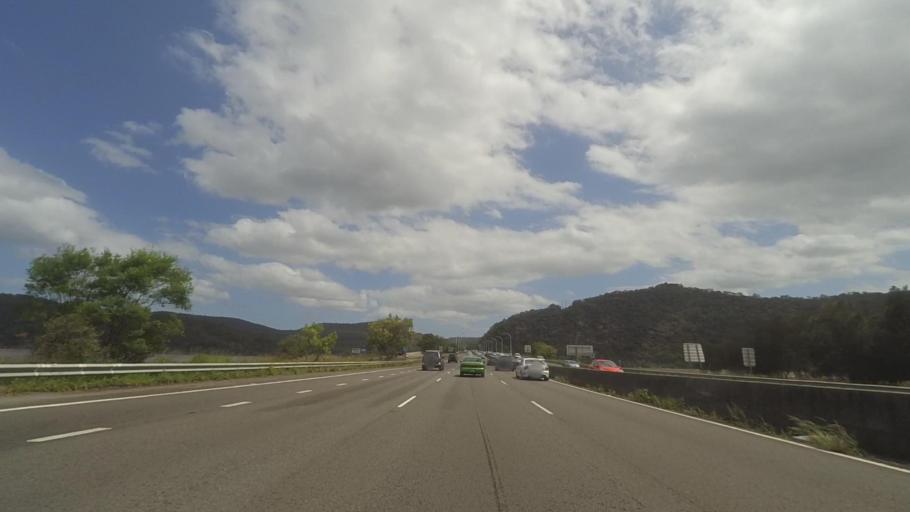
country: AU
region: New South Wales
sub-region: Hornsby Shire
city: Berowra
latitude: -33.5338
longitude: 151.2002
